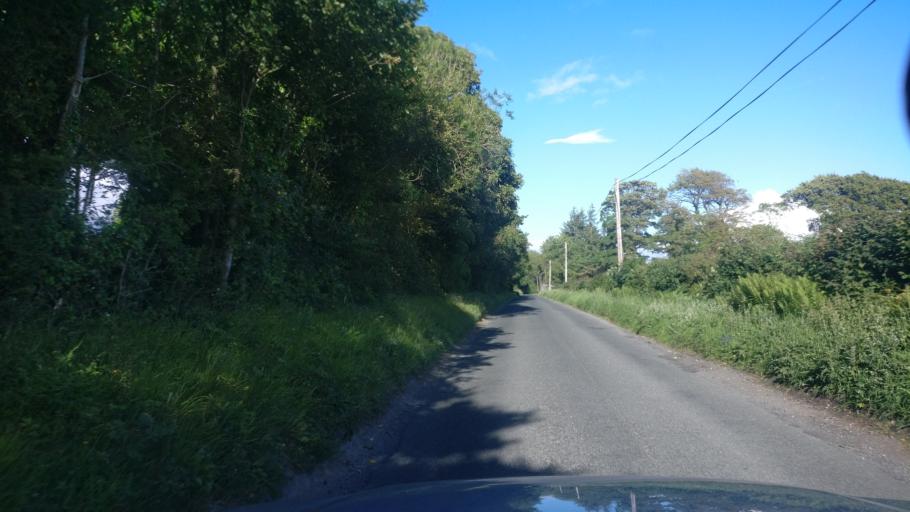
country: IE
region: Connaught
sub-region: County Galway
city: Ballinasloe
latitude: 53.2278
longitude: -8.2367
